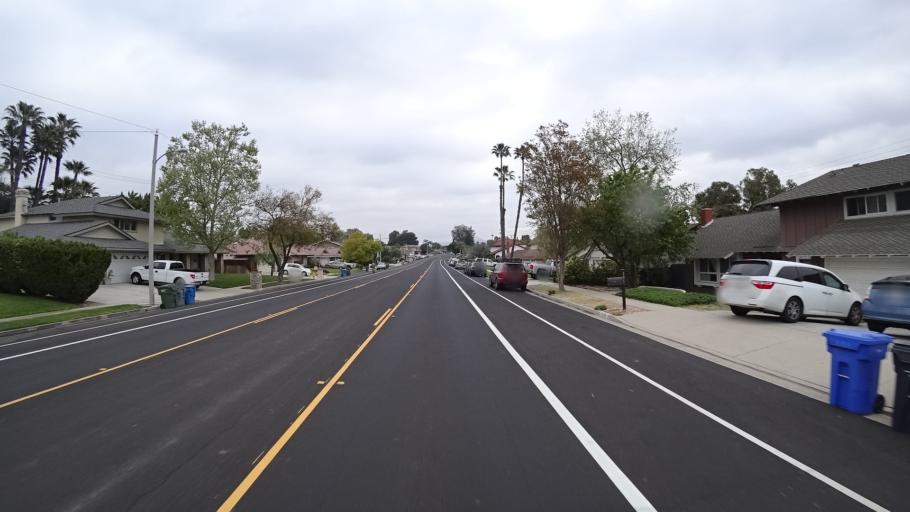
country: US
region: California
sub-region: Ventura County
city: Thousand Oaks
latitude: 34.2127
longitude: -118.8814
